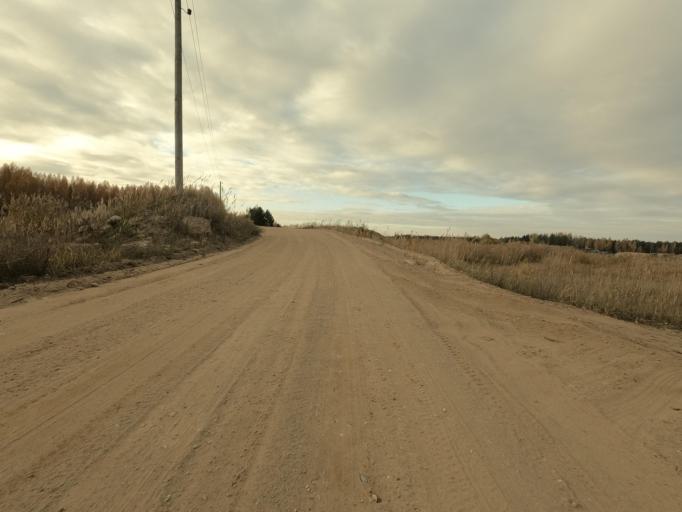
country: RU
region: Leningrad
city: Priladozhskiy
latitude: 59.7110
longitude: 31.3588
